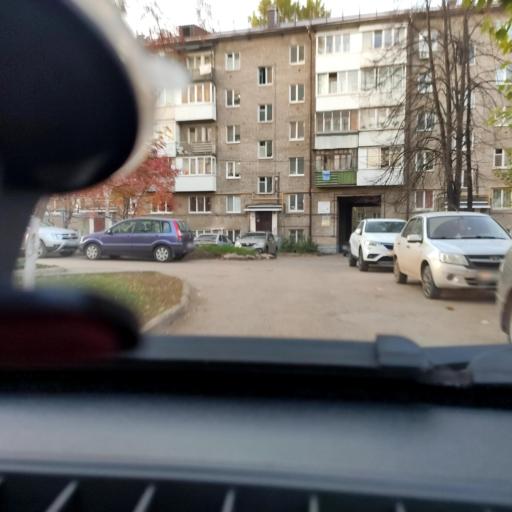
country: RU
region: Bashkortostan
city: Ufa
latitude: 54.7335
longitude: 55.9735
